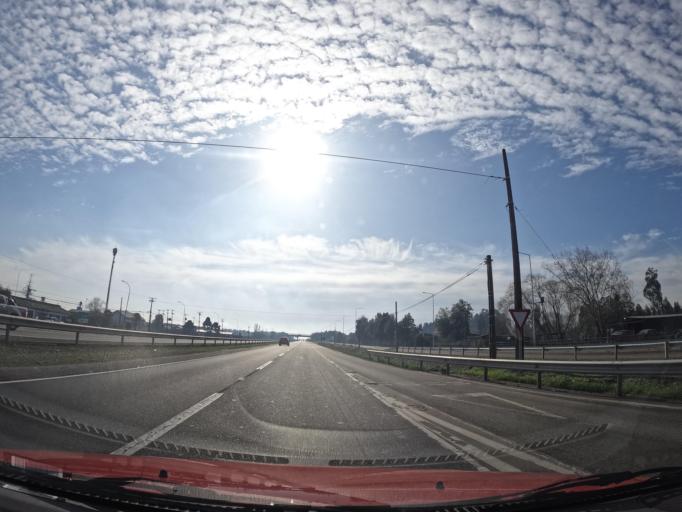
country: CL
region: Biobio
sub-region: Provincia de Nuble
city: San Carlos
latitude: -36.4189
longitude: -71.9459
